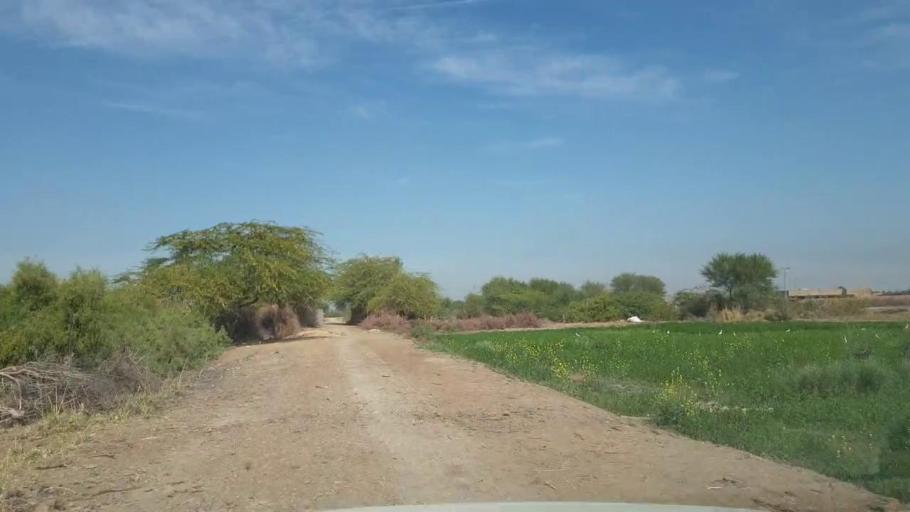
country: PK
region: Sindh
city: Mirpur Khas
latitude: 25.6248
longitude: 69.1960
